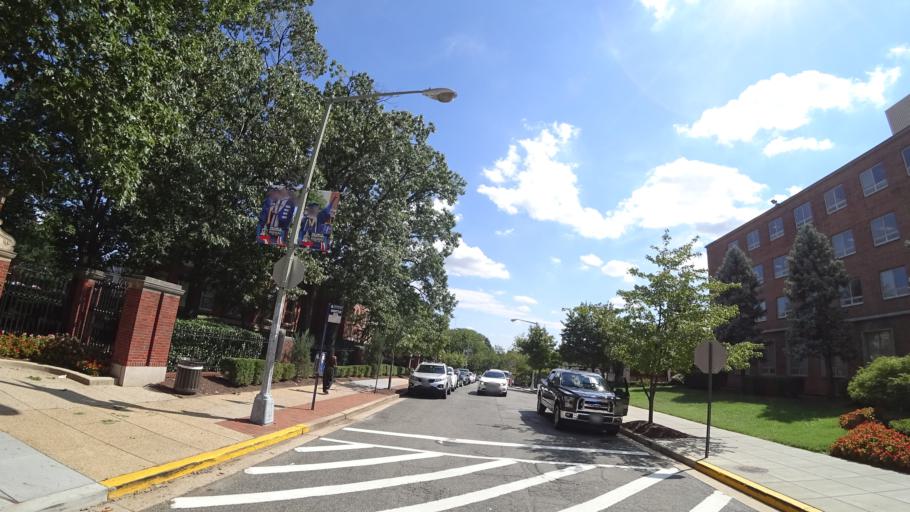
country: US
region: Washington, D.C.
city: Washington, D.C.
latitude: 38.9232
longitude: -77.0212
